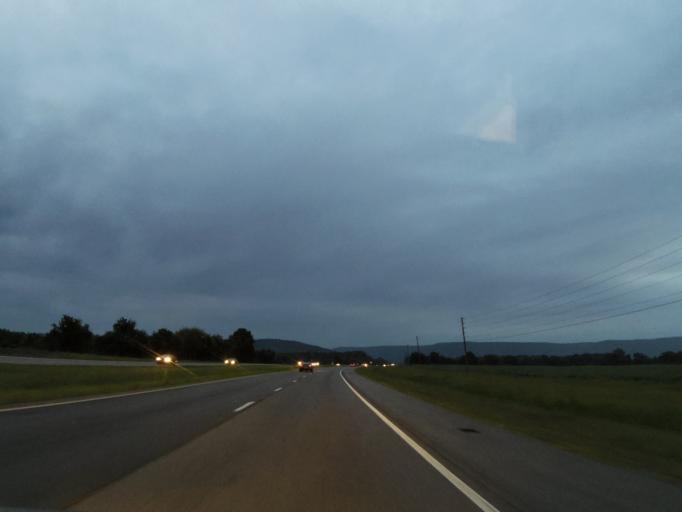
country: US
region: Alabama
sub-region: Madison County
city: Owens Cross Roads
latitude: 34.7296
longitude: -86.4208
